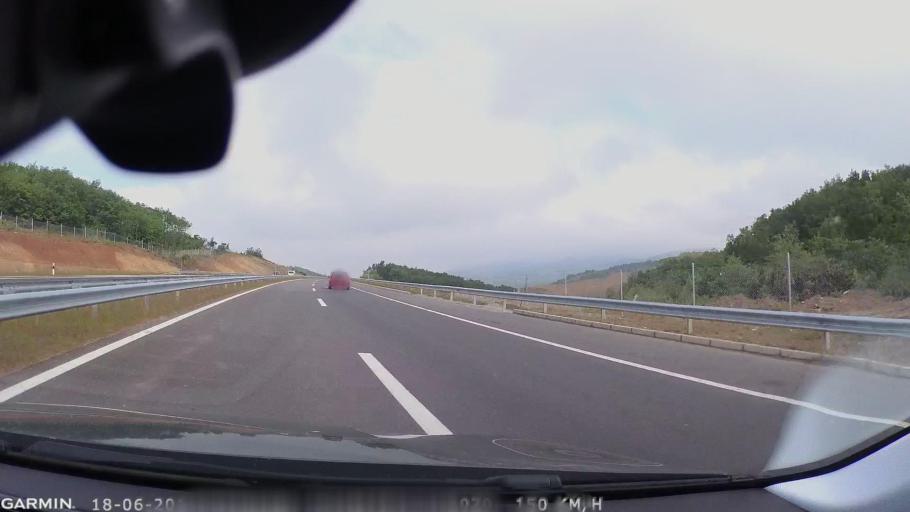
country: MK
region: Sveti Nikole
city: Gorobinci
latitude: 41.9202
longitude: 21.8674
